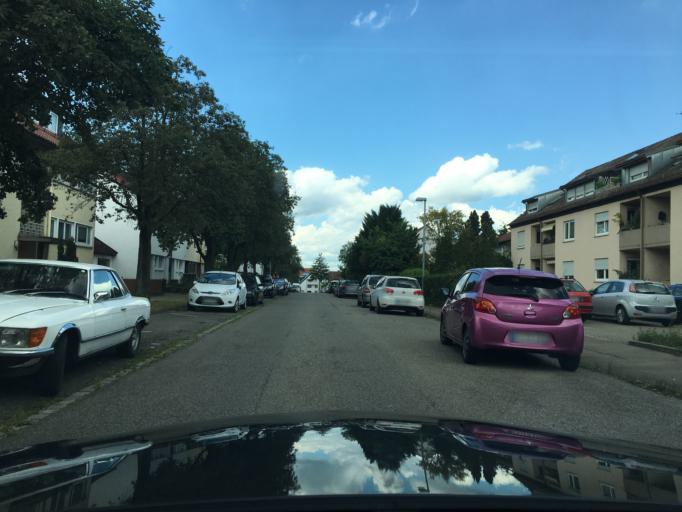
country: DE
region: Baden-Wuerttemberg
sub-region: Regierungsbezirk Stuttgart
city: Filderstadt
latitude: 48.6992
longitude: 9.2143
